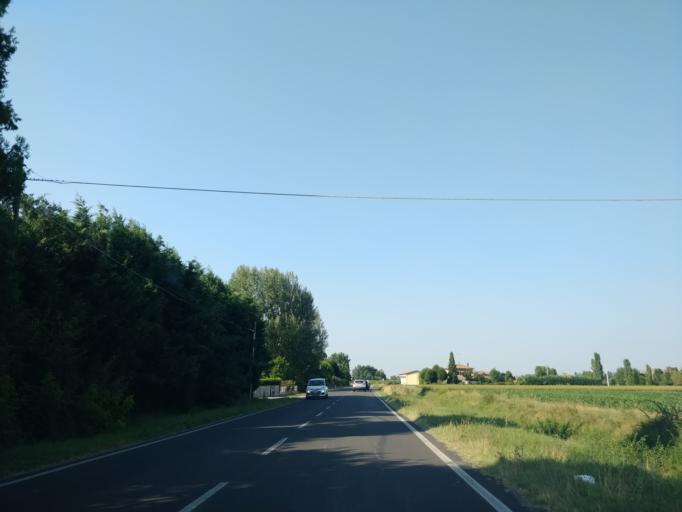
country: IT
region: Emilia-Romagna
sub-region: Provincia di Bologna
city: Argelato
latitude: 44.6303
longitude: 11.3419
